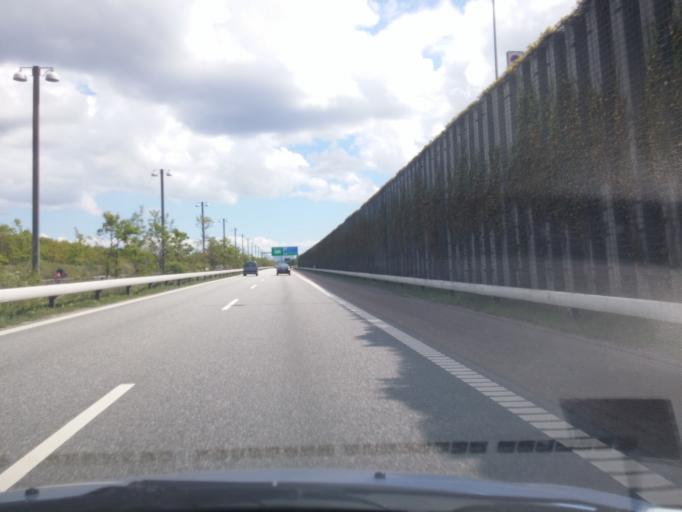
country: DK
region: Capital Region
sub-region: Tarnby Kommune
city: Tarnby
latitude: 55.6299
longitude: 12.6225
